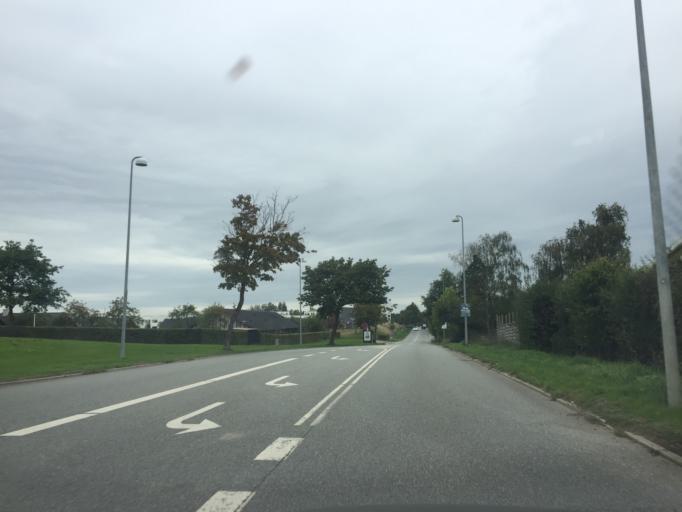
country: DK
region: Capital Region
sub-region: Hillerod Kommune
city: Hillerod
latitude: 55.9367
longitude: 12.2634
